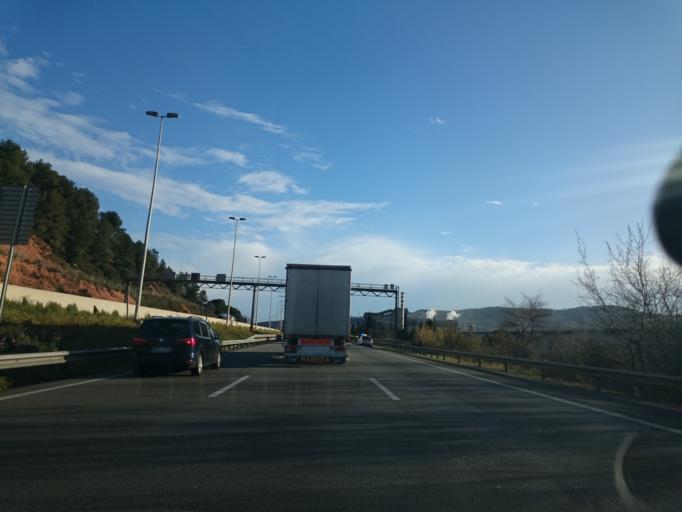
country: ES
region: Catalonia
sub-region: Provincia de Barcelona
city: Castellbisbal
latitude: 41.4604
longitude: 1.9807
